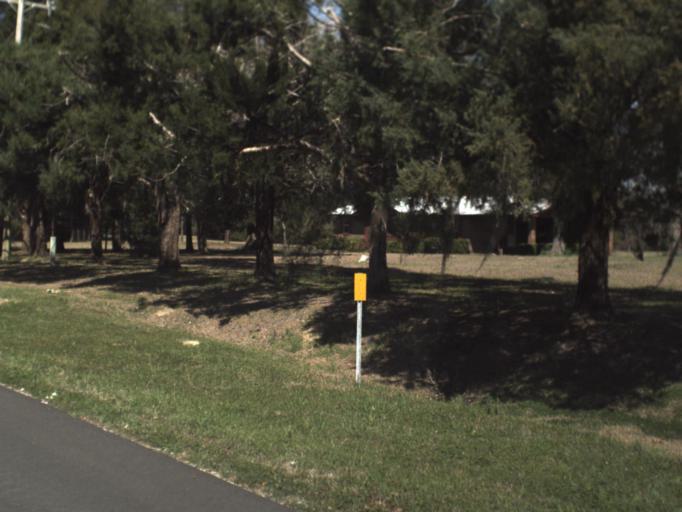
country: US
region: Florida
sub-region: Jackson County
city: Malone
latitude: 30.8332
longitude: -85.0561
